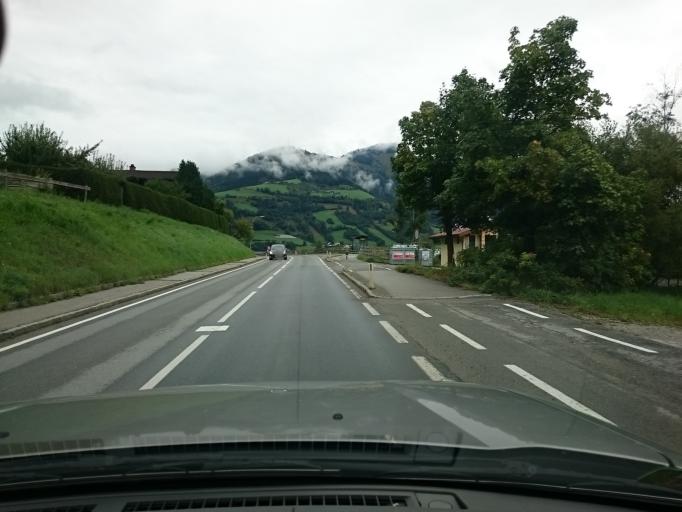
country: AT
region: Salzburg
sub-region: Politischer Bezirk Zell am See
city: Bruck an der Grossglocknerstrasse
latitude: 47.2719
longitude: 12.8256
